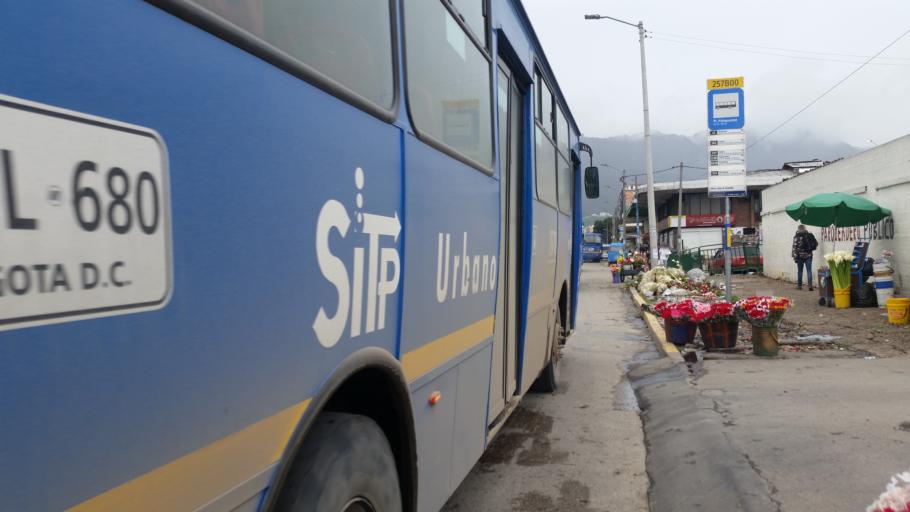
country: CO
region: Bogota D.C.
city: Bogota
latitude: 4.6158
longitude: -74.0856
